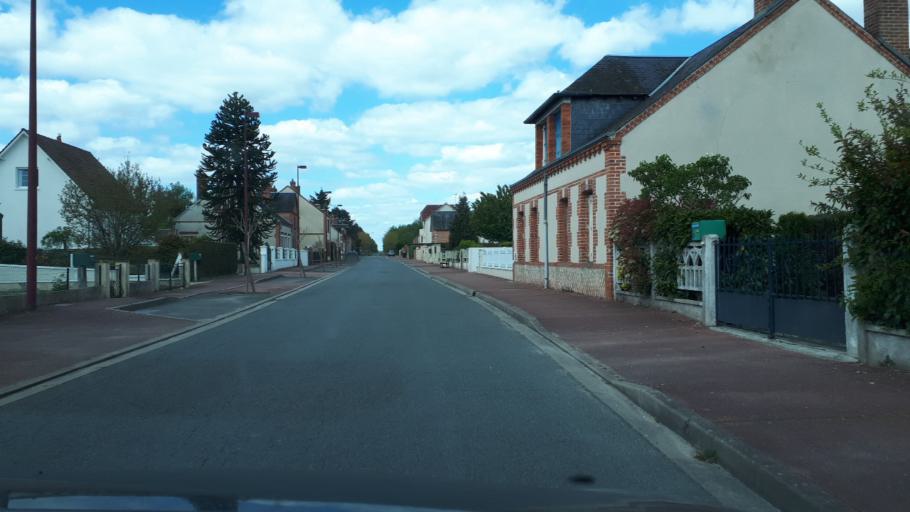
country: FR
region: Centre
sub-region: Departement du Loir-et-Cher
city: Nouan-le-Fuzelier
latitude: 47.5347
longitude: 2.0300
